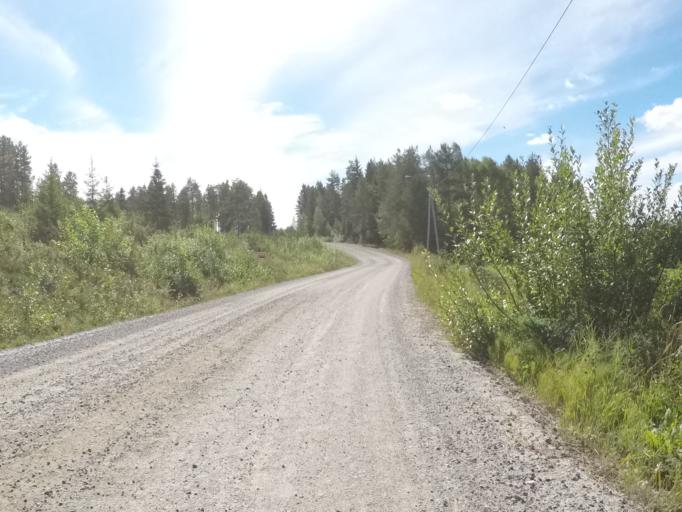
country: SE
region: Vaesterbotten
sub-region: Robertsfors Kommun
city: Robertsfors
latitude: 64.0039
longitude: 20.8127
